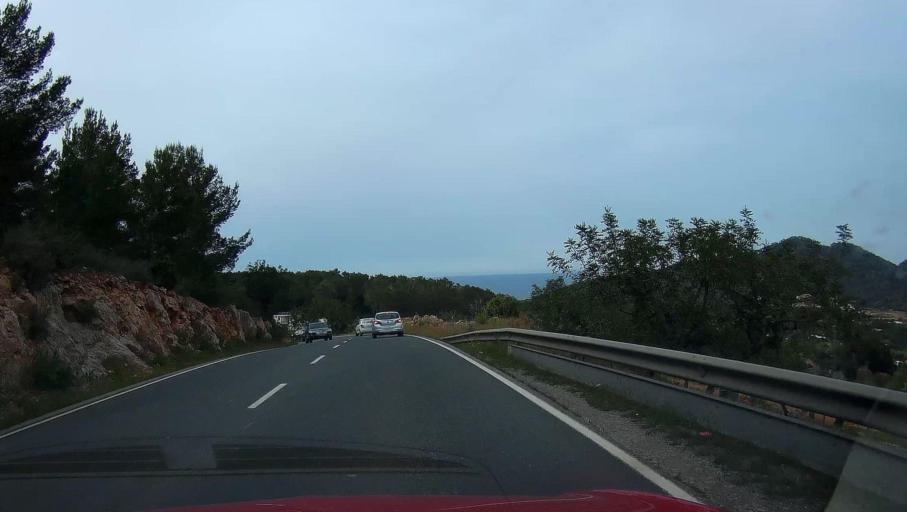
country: ES
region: Balearic Islands
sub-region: Illes Balears
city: Sant Joan de Labritja
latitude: 39.0812
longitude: 1.4975
